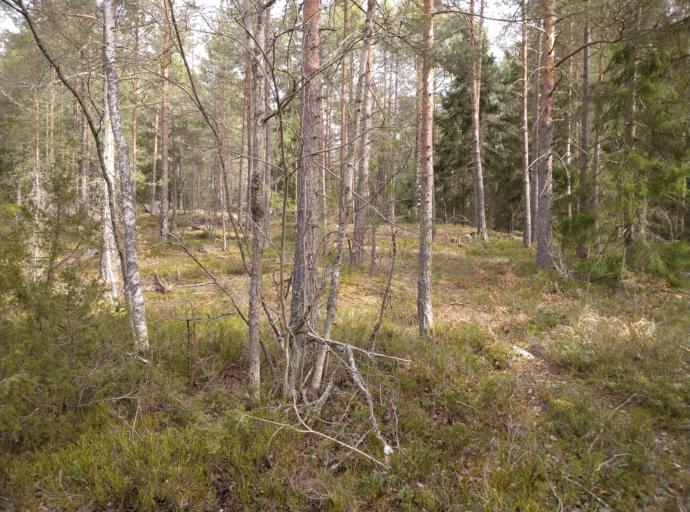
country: SE
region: Stockholm
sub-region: Nacka Kommun
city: Fisksatra
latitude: 59.2896
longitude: 18.2402
